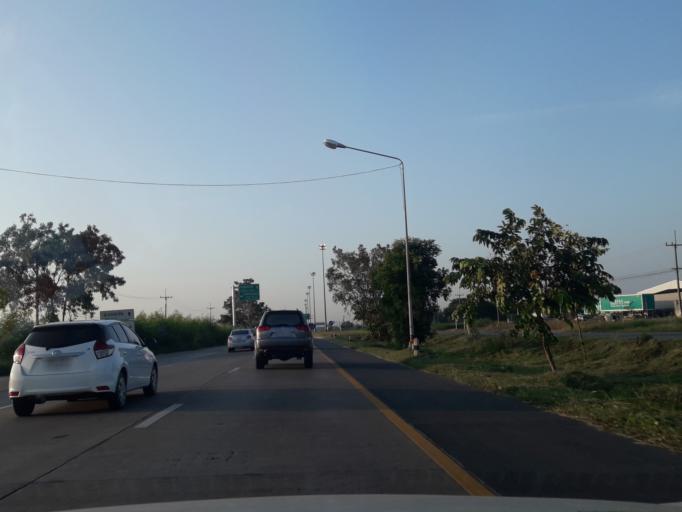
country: TH
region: Phra Nakhon Si Ayutthaya
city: Phra Nakhon Si Ayutthaya
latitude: 14.3106
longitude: 100.5267
